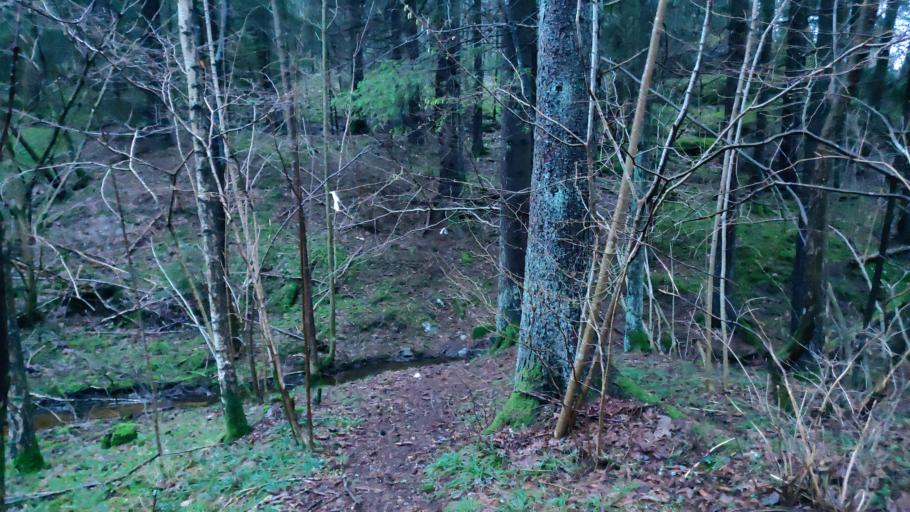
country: SE
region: Vaestra Goetaland
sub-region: Uddevalla Kommun
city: Uddevalla
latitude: 58.3409
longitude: 11.9366
